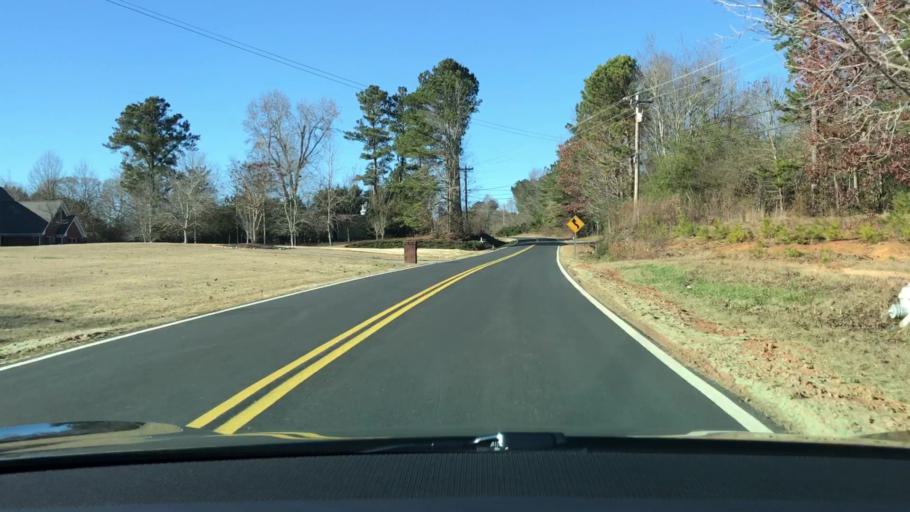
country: US
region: Georgia
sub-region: Barrow County
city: Auburn
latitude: 34.0798
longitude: -83.8655
